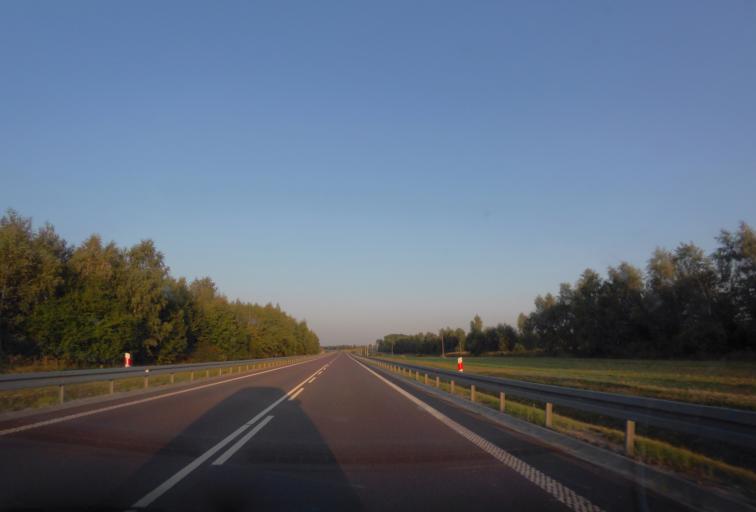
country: PL
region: Lublin Voivodeship
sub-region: Powiat bilgorajski
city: Frampol
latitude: 50.6770
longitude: 22.6652
